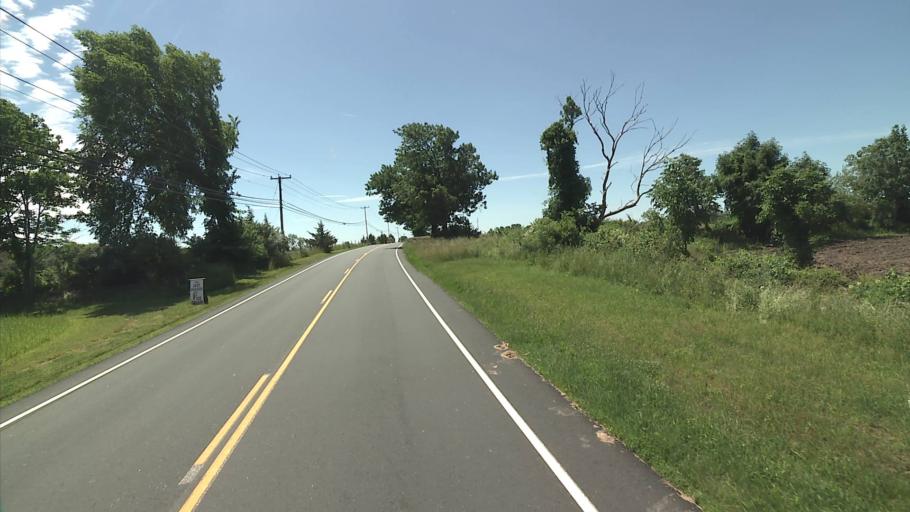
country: US
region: Connecticut
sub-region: Windham County
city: Moosup
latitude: 41.6713
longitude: -71.8492
